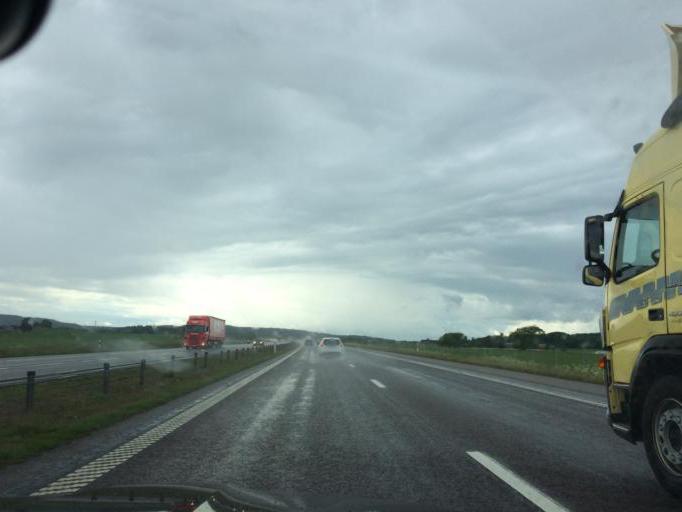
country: SE
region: Halland
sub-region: Halmstads Kommun
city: Getinge
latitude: 56.7976
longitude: 12.7762
